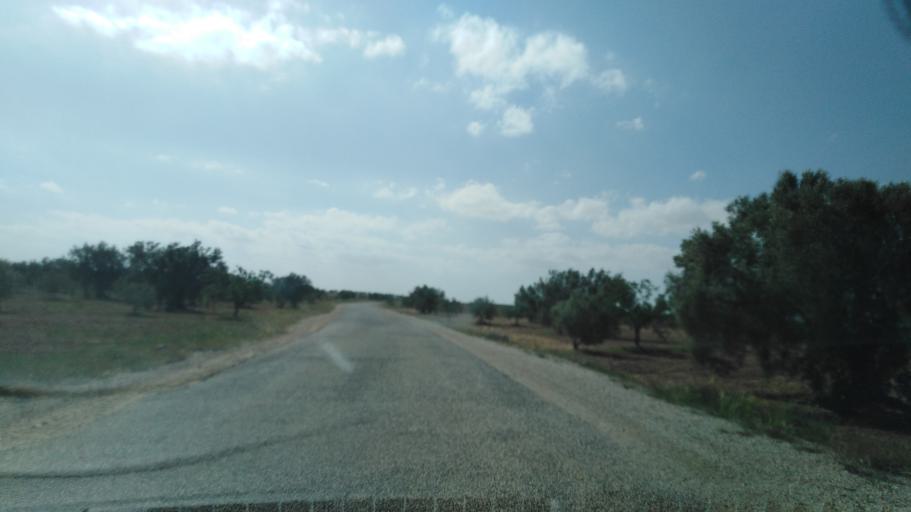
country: TN
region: Safaqis
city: Bi'r `Ali Bin Khalifah
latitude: 34.7774
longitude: 10.3605
